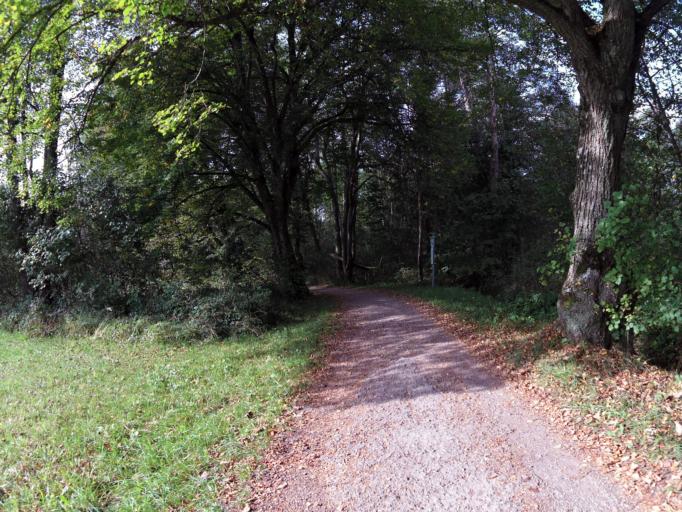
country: DE
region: Bavaria
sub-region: Upper Bavaria
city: Bernried
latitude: 47.8811
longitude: 11.2752
